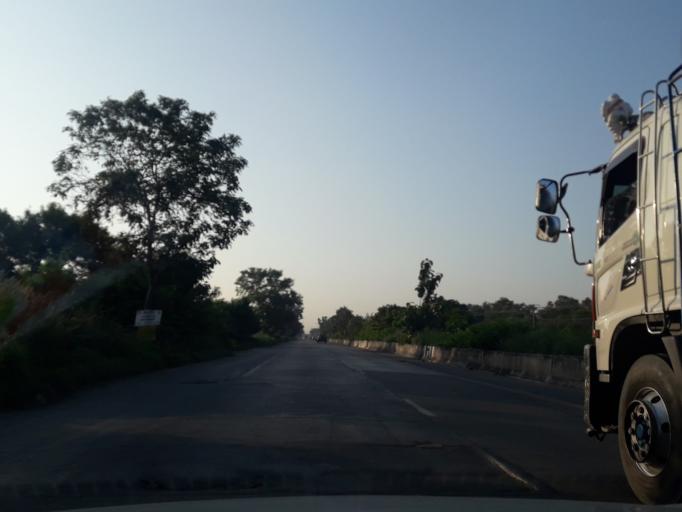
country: TH
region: Phra Nakhon Si Ayutthaya
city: Bang Pa-in
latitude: 14.1808
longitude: 100.5581
